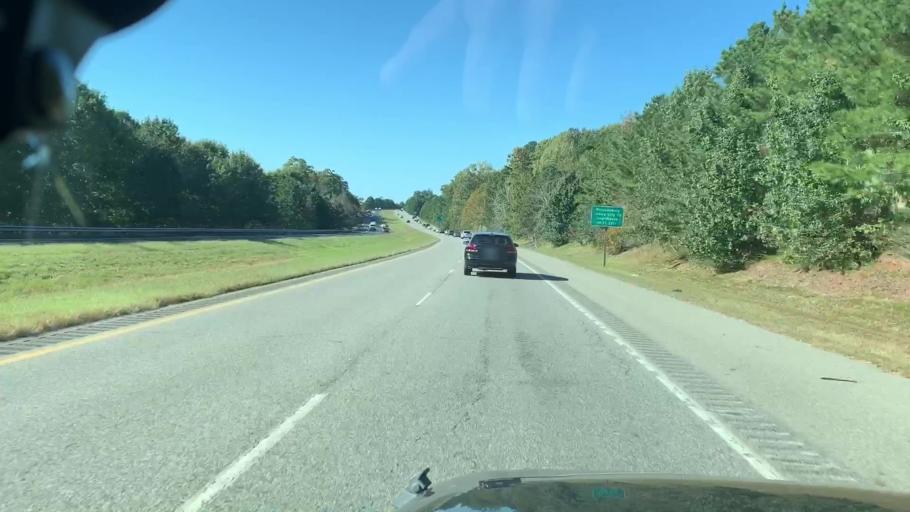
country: US
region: Virginia
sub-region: James City County
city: Williamsburg
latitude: 37.2673
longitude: -76.7444
